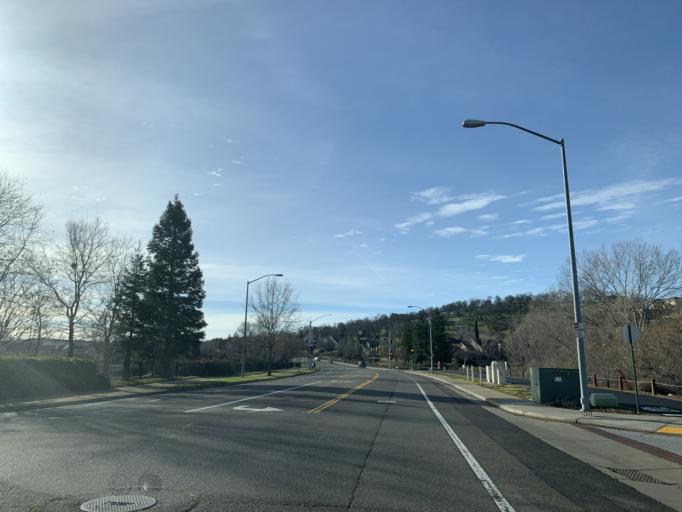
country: US
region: California
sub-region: El Dorado County
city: El Dorado Hills
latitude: 38.6752
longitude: -121.1106
